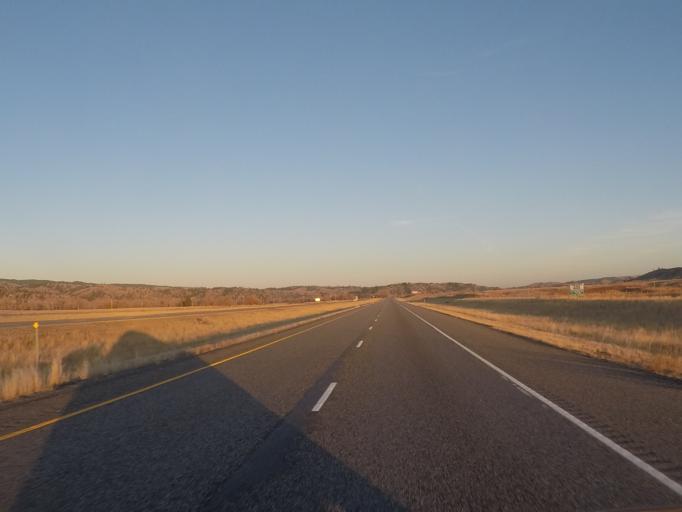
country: US
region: Montana
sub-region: Sweet Grass County
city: Big Timber
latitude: 45.7337
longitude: -109.7028
